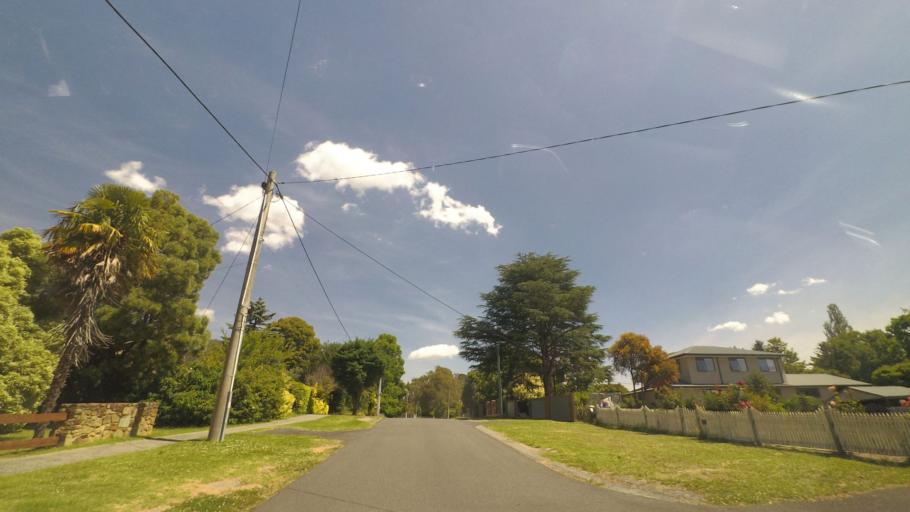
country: AU
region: Victoria
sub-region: Yarra Ranges
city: Montrose
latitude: -37.8053
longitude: 145.3440
